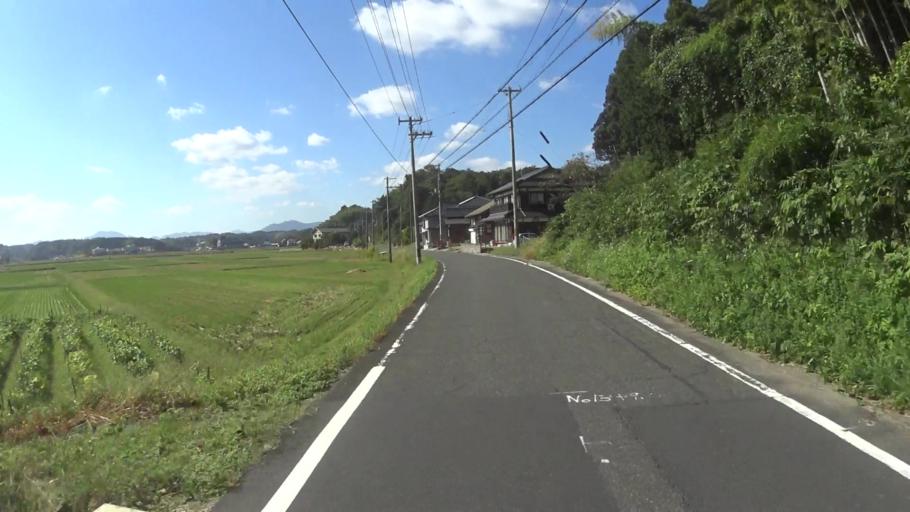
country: JP
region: Kyoto
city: Miyazu
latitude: 35.6791
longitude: 135.0866
